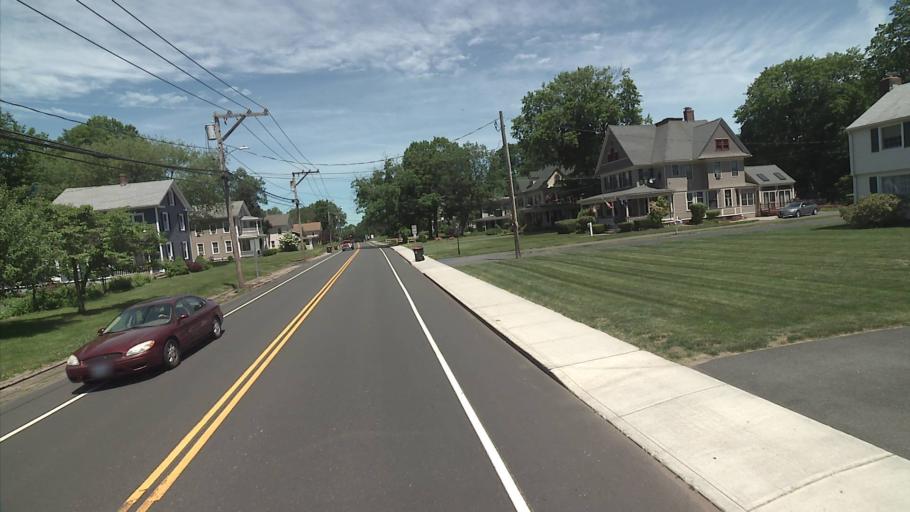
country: US
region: Connecticut
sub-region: Hartford County
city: Plainville
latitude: 41.5925
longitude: -72.8752
